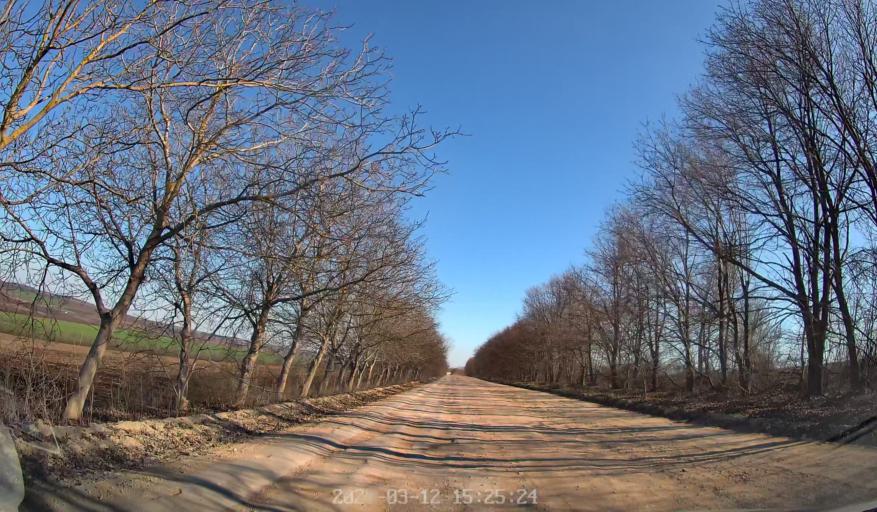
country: MD
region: Chisinau
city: Ciorescu
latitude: 47.1828
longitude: 28.9183
